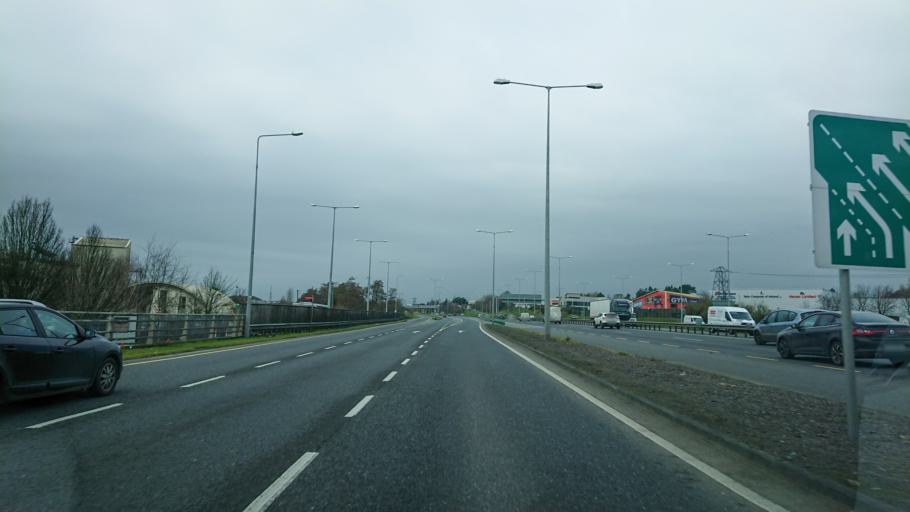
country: IE
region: Munster
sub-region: County Cork
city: Cork
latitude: 51.8740
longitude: -8.4766
